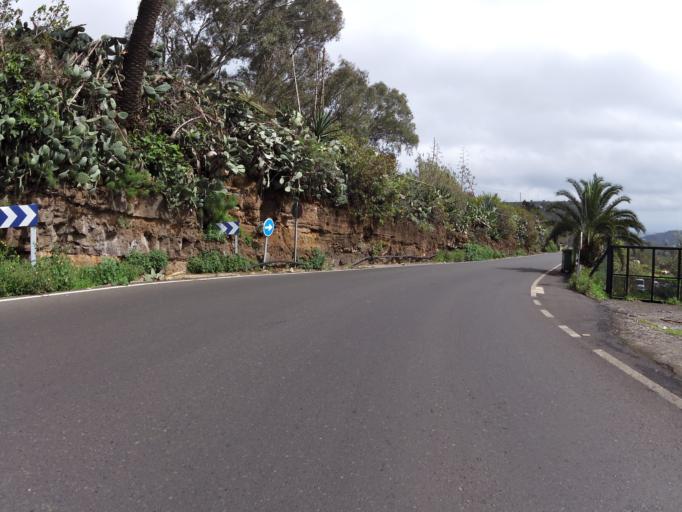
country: ES
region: Canary Islands
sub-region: Provincia de Las Palmas
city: Teror
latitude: 28.0828
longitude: -15.5428
